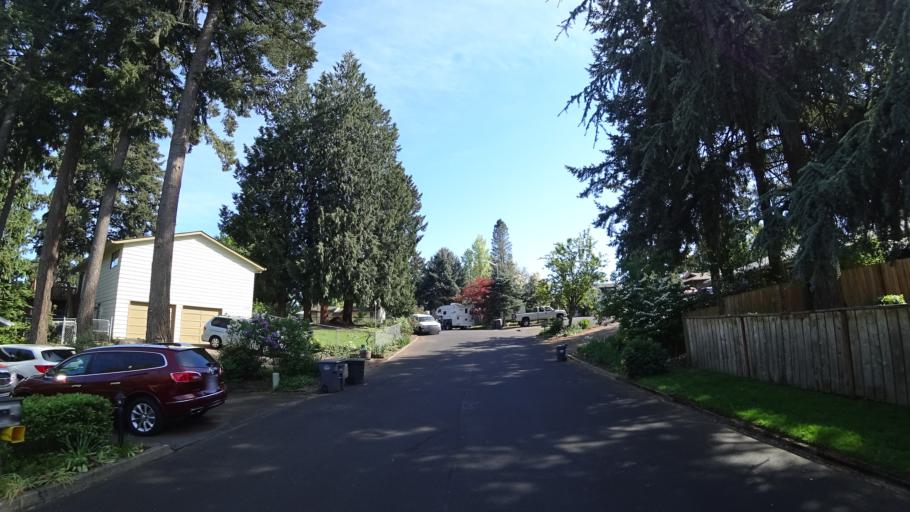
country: US
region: Oregon
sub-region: Washington County
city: Hillsboro
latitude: 45.5163
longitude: -122.9604
